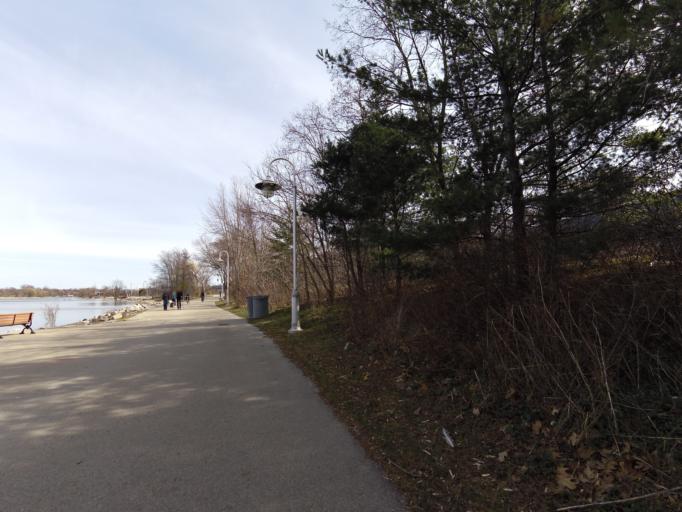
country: CA
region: Ontario
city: Hamilton
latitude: 43.2719
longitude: -79.8840
